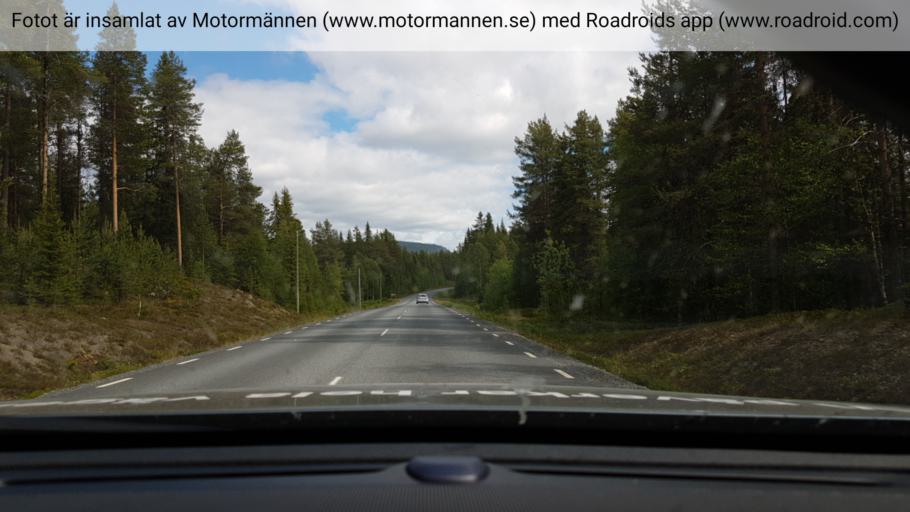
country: SE
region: Vaesterbotten
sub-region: Sorsele Kommun
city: Sorsele
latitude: 65.6864
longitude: 17.3303
